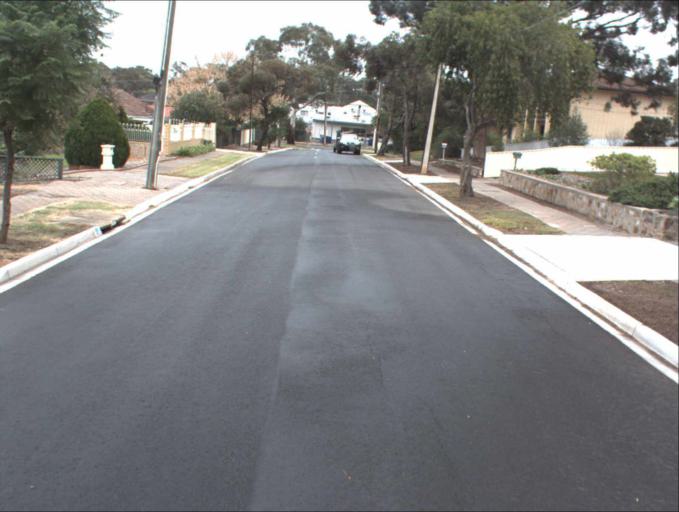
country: AU
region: South Australia
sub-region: Campbelltown
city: Paradise
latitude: -34.8616
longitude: 138.6640
